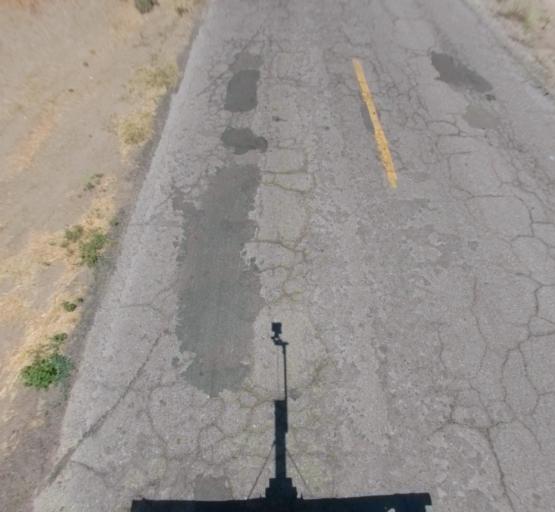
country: US
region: California
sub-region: Madera County
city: Parkwood
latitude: 36.8606
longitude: -120.1103
